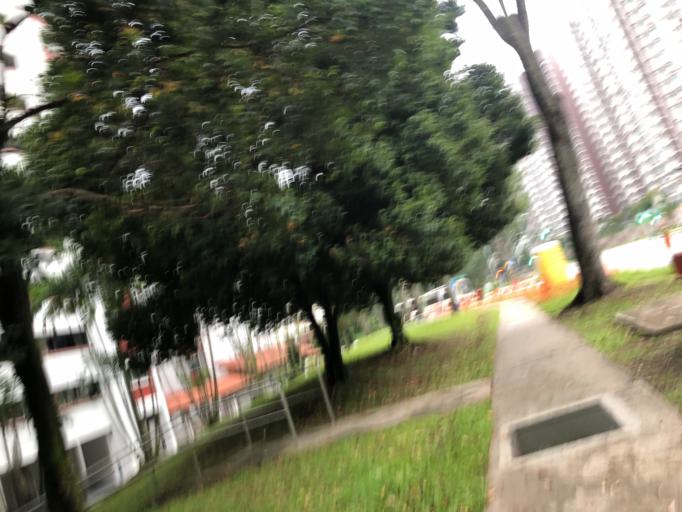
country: MY
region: Johor
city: Johor Bahru
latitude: 1.3521
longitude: 103.7462
